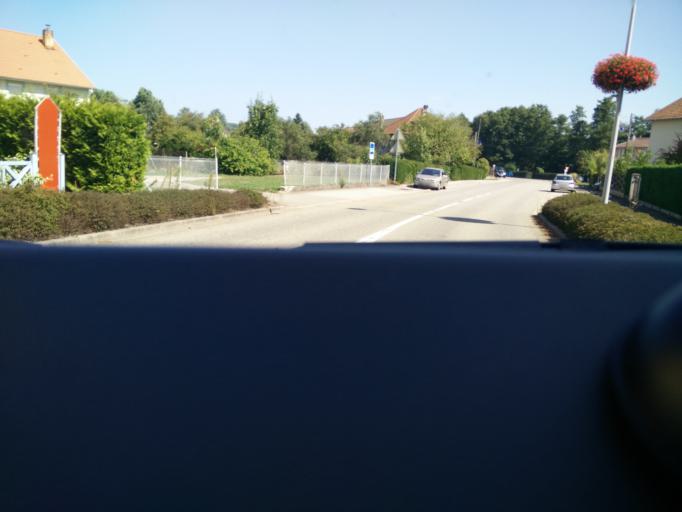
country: FR
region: Lorraine
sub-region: Departement des Vosges
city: Saulcy-sur-Meurthe
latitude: 48.2374
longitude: 6.9522
